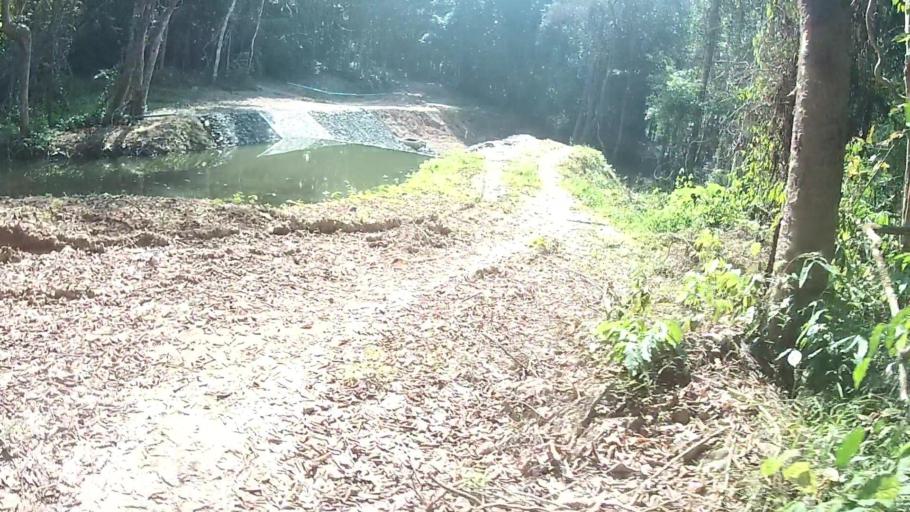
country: TH
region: Chiang Mai
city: San Sai
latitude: 18.9496
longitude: 99.0644
